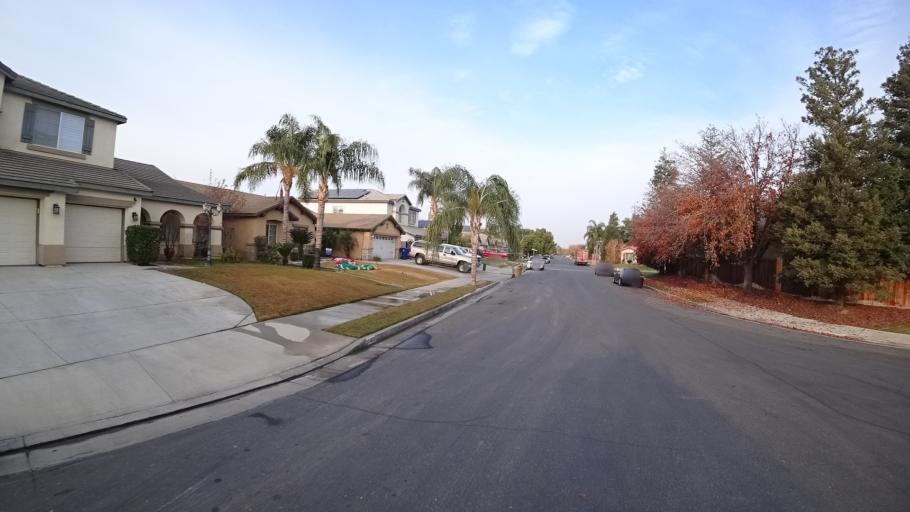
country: US
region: California
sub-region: Kern County
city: Greenacres
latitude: 35.4168
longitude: -119.1182
